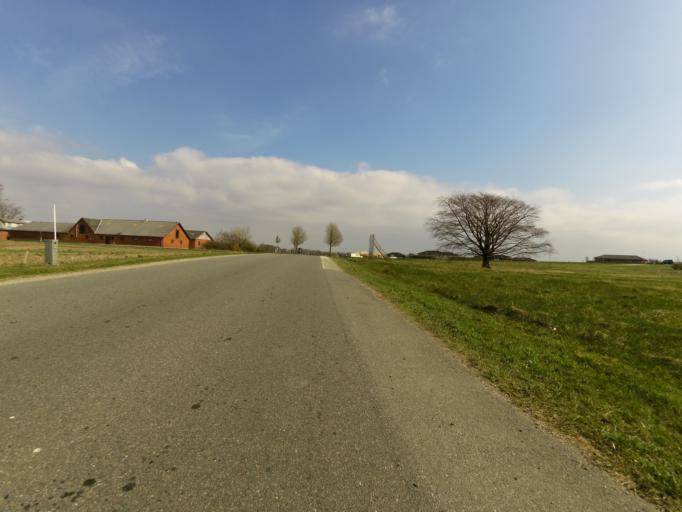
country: DK
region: Central Jutland
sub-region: Struer Kommune
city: Struer
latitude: 56.4390
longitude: 8.6471
